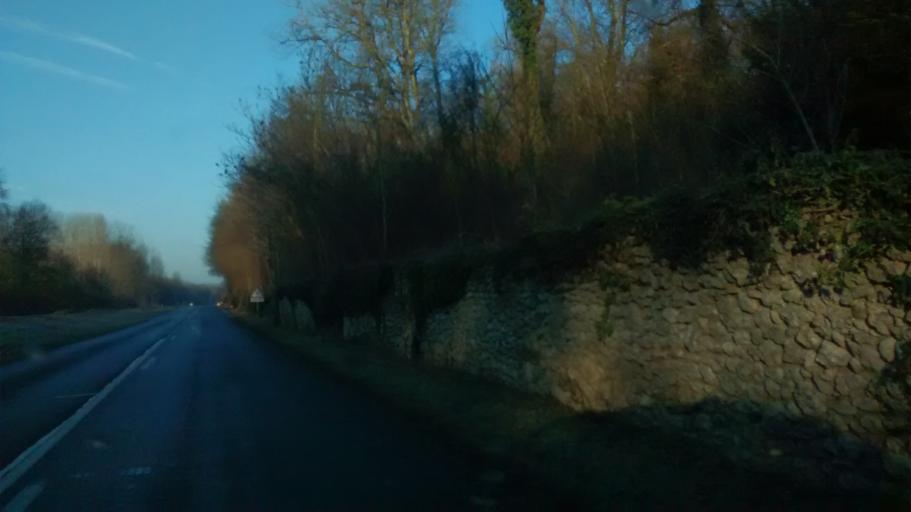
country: FR
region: Centre
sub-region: Departement d'Indre-et-Loire
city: Veigne
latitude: 47.2885
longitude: 0.7609
